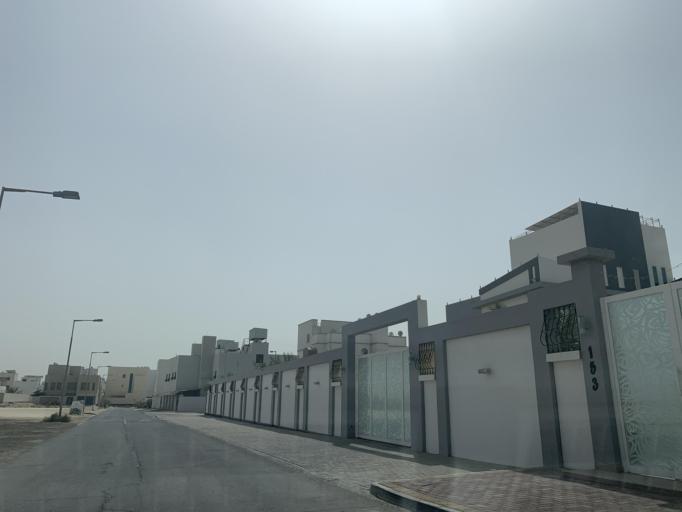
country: BH
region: Central Governorate
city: Madinat Hamad
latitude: 26.1533
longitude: 50.5112
